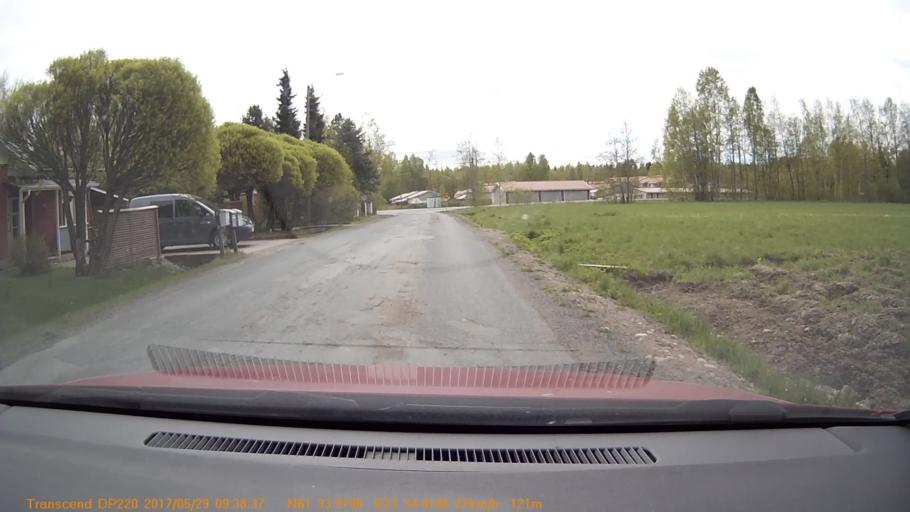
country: FI
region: Pirkanmaa
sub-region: Tampere
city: Yloejaervi
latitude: 61.5663
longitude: 23.5736
